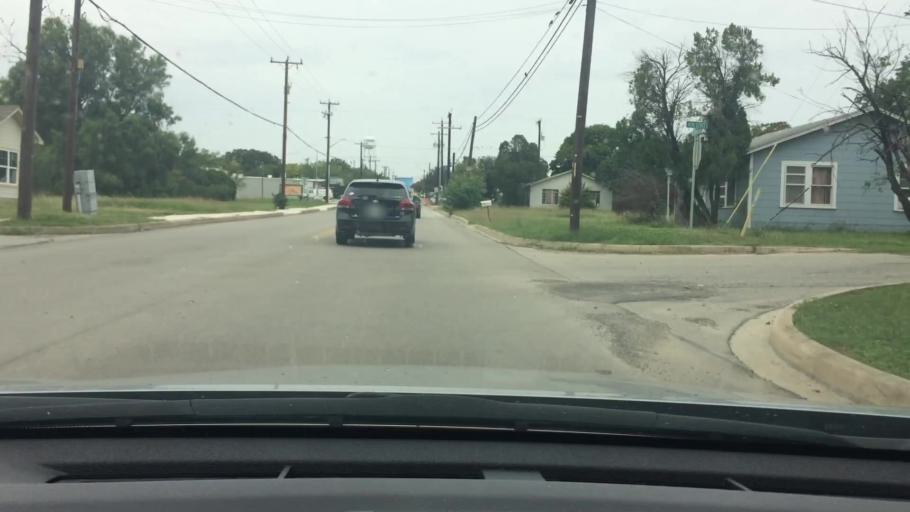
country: US
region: Texas
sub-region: Bexar County
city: Converse
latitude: 29.5214
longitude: -98.3188
